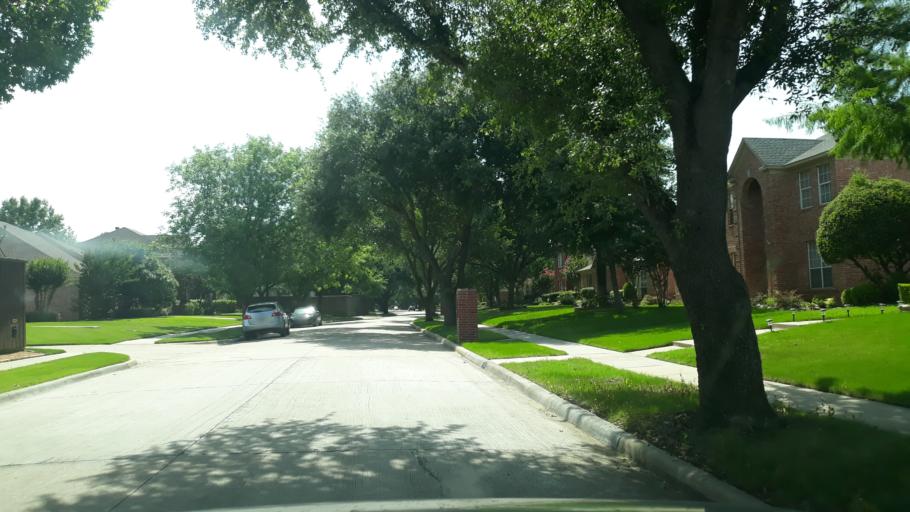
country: US
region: Texas
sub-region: Dallas County
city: Coppell
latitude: 32.9673
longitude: -97.0017
